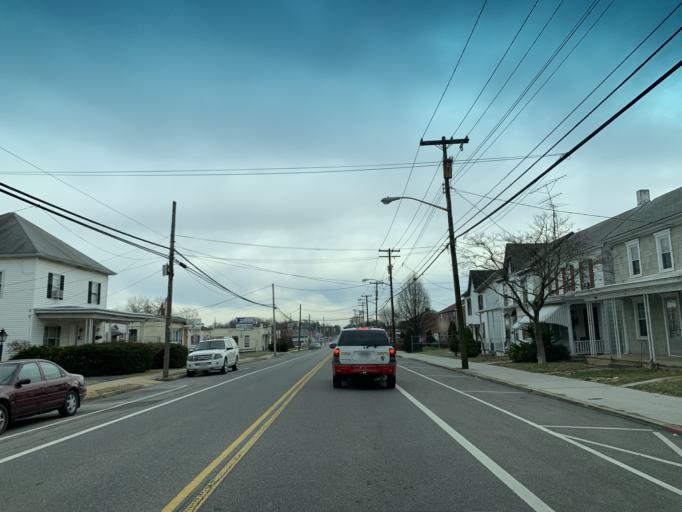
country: US
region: Maryland
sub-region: Washington County
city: Hagerstown
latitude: 39.6304
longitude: -77.7163
